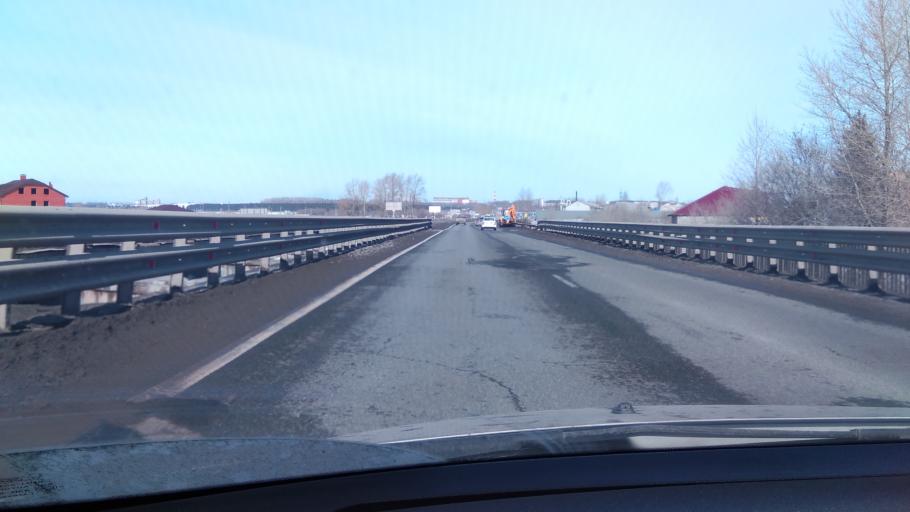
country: RU
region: Perm
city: Froly
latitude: 57.9168
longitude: 56.2647
